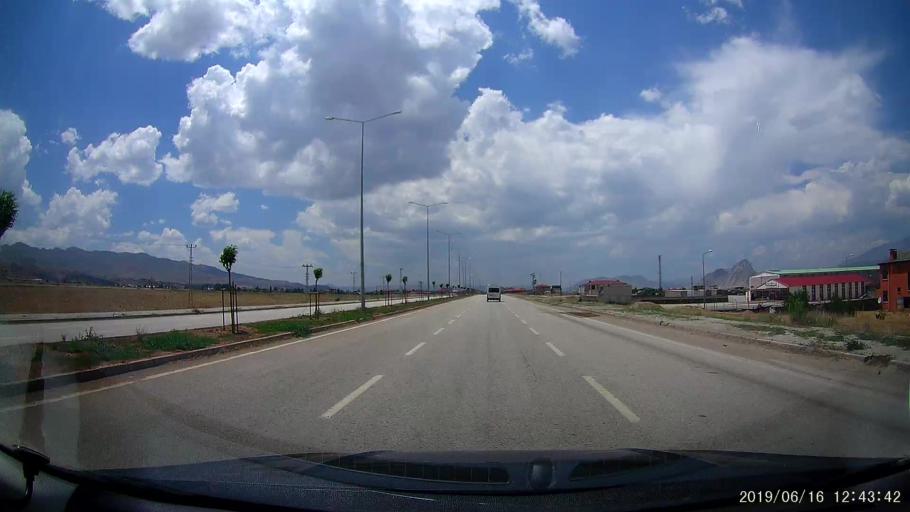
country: TR
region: Agri
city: Dogubayazit
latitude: 39.5580
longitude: 44.1123
